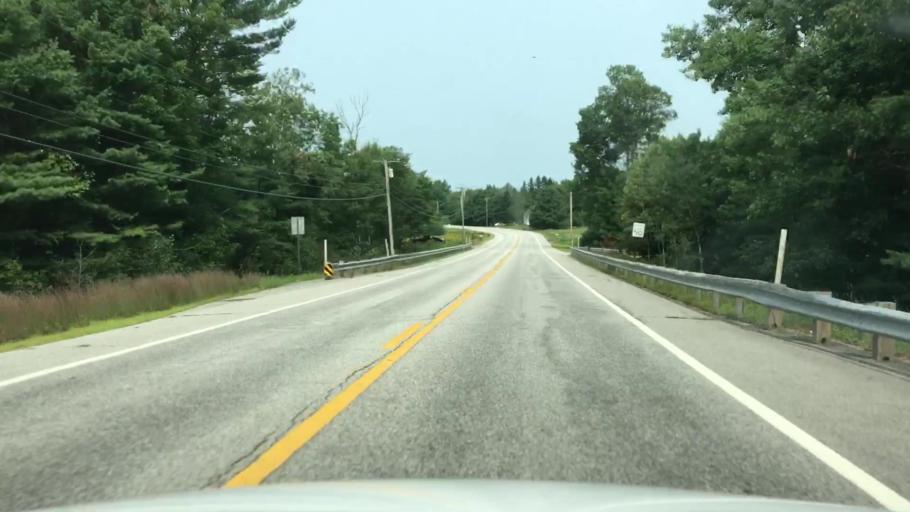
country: US
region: Maine
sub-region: Androscoggin County
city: Livermore Falls
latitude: 44.4433
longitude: -70.1504
